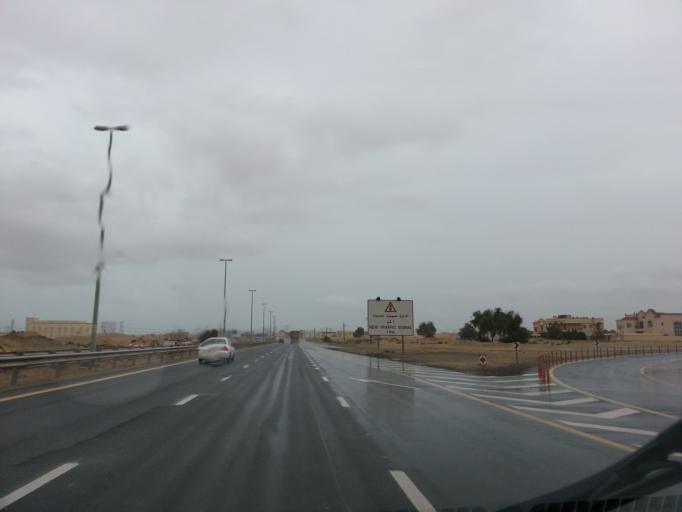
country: AE
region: Dubai
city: Dubai
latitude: 25.0620
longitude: 55.2211
